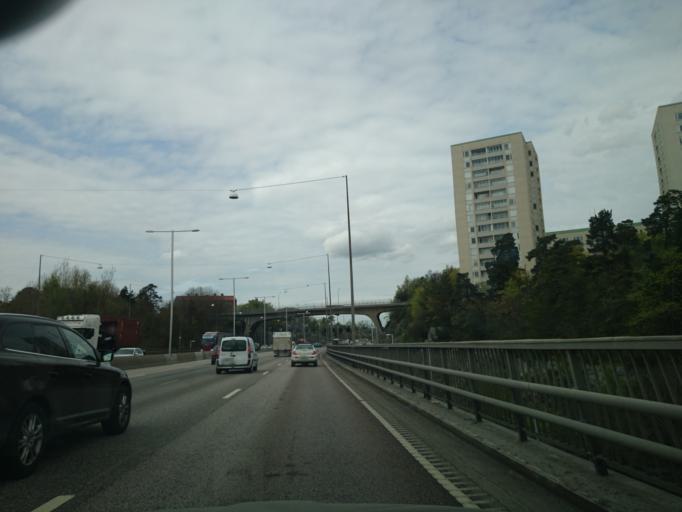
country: SE
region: Stockholm
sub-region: Stockholms Kommun
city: Arsta
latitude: 59.3064
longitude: 18.0138
